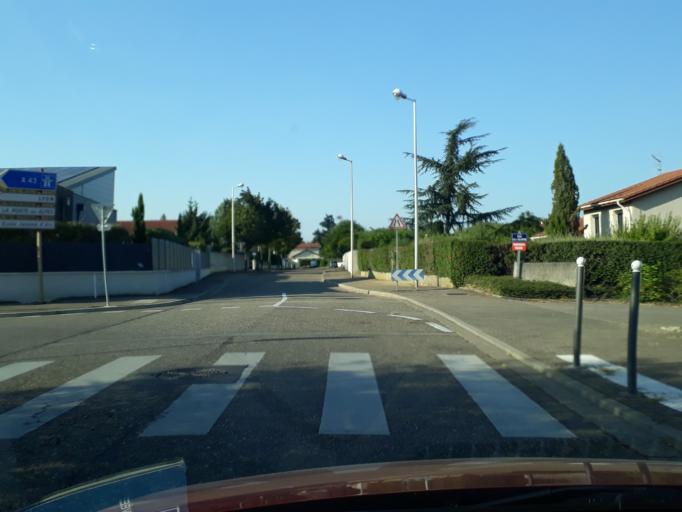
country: FR
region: Rhone-Alpes
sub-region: Departement du Rhone
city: Saint-Priest
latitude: 45.7065
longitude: 4.9462
